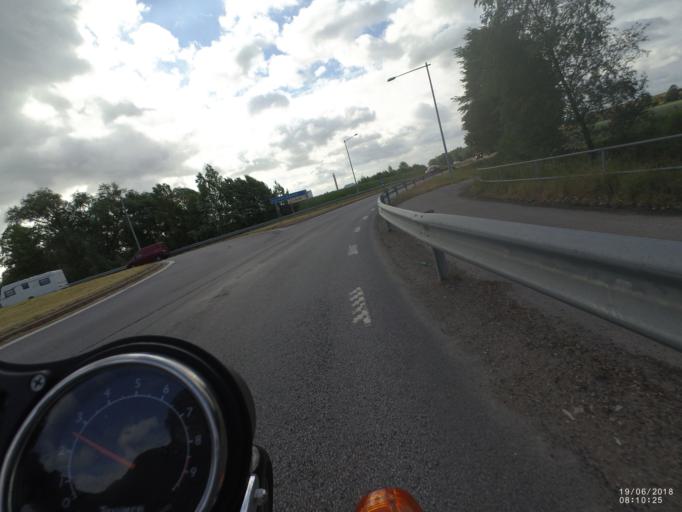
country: SE
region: Soedermanland
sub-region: Nykopings Kommun
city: Nykoping
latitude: 58.7491
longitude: 16.9891
